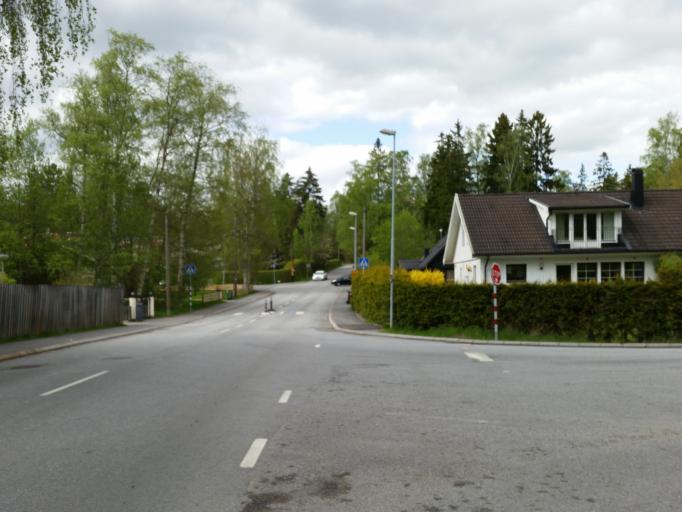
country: SE
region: Stockholm
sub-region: Sollentuna Kommun
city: Sollentuna
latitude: 59.4594
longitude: 17.9489
